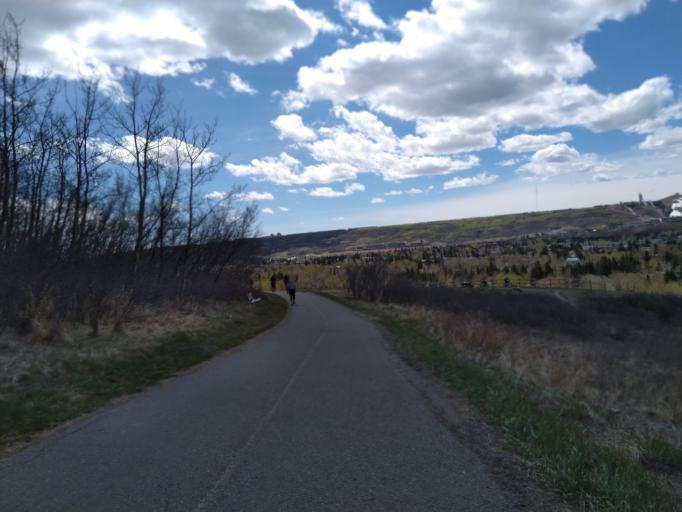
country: CA
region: Alberta
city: Calgary
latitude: 51.0990
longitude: -114.1902
